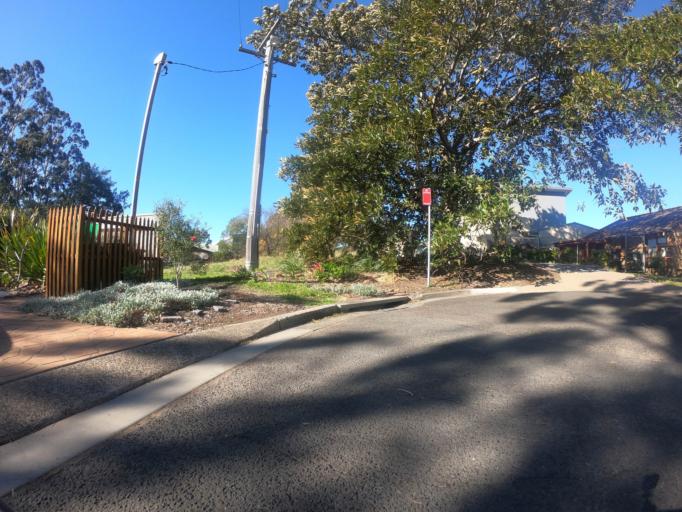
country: AU
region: New South Wales
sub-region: Wollongong
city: Cordeaux Heights
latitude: -34.4347
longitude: 150.8463
